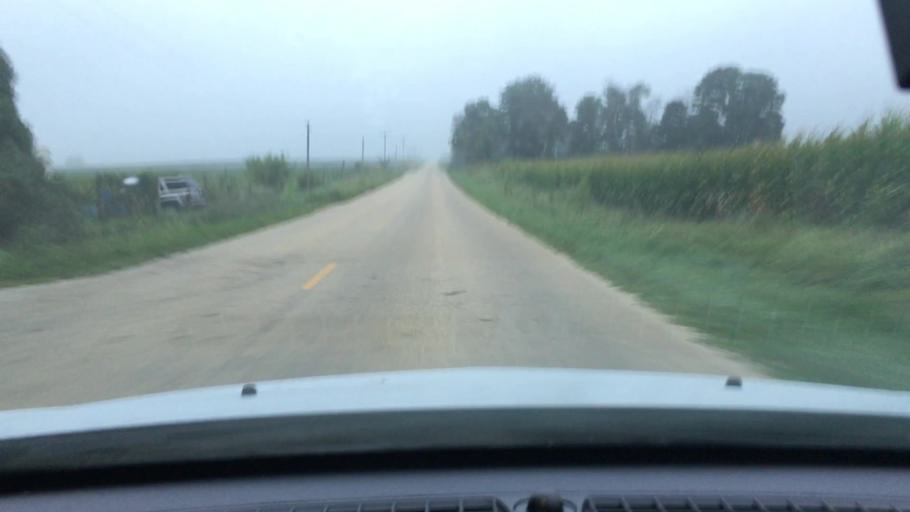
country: US
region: Illinois
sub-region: DeKalb County
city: Malta
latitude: 41.8669
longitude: -88.9615
